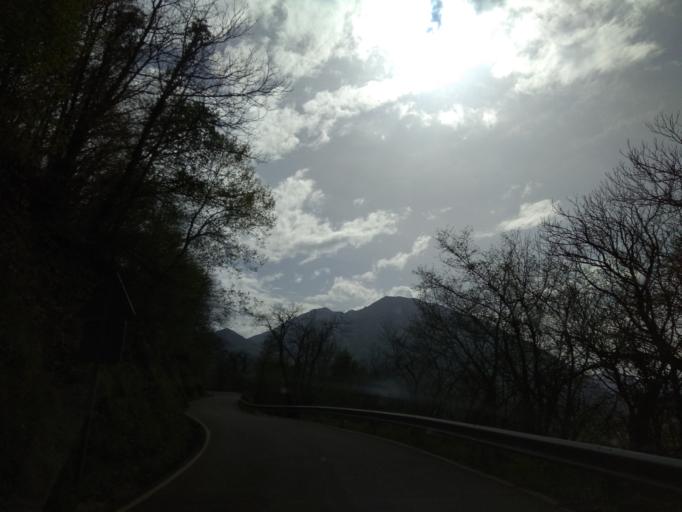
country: ES
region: Cantabria
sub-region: Provincia de Cantabria
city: Tresviso
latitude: 43.2543
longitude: -4.5692
